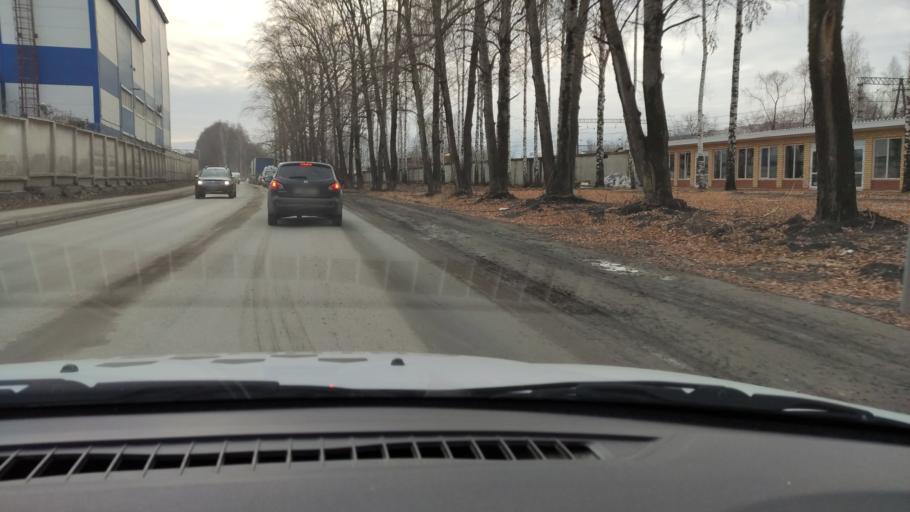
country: RU
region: Perm
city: Perm
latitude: 57.9586
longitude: 56.2098
